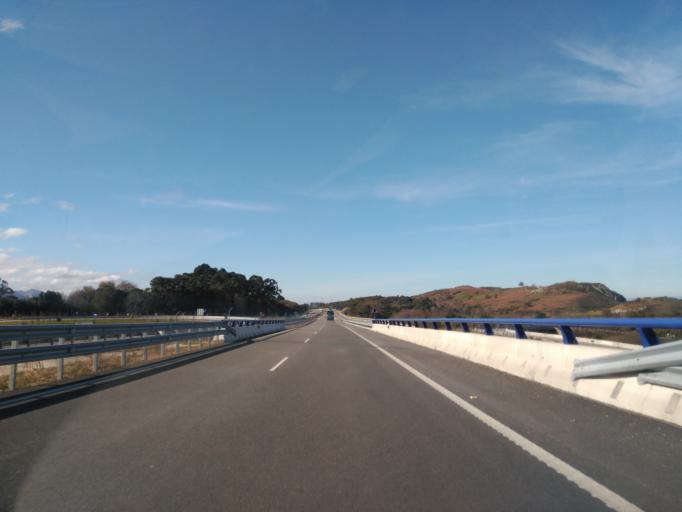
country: ES
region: Asturias
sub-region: Province of Asturias
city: Llanes
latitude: 43.3959
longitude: -4.6531
